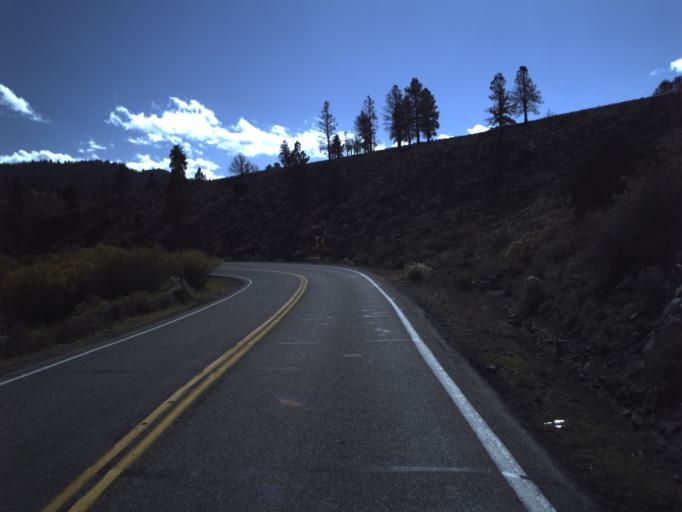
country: US
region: Utah
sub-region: Garfield County
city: Panguitch
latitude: 37.7340
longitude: -112.6064
